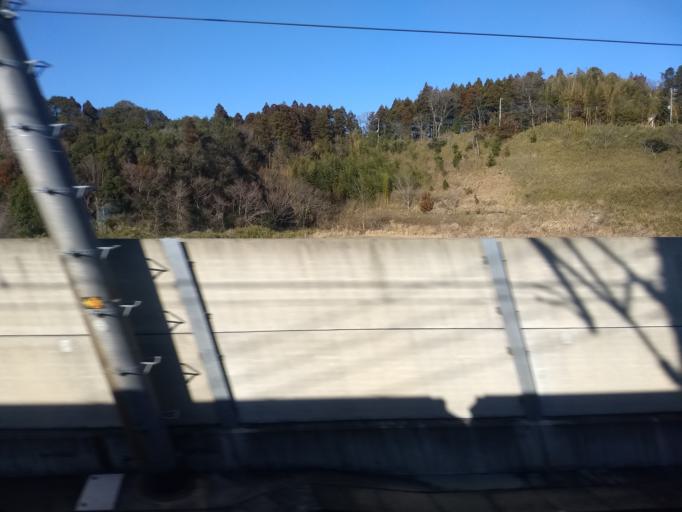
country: JP
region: Chiba
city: Sakura
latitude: 35.7826
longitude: 140.2309
